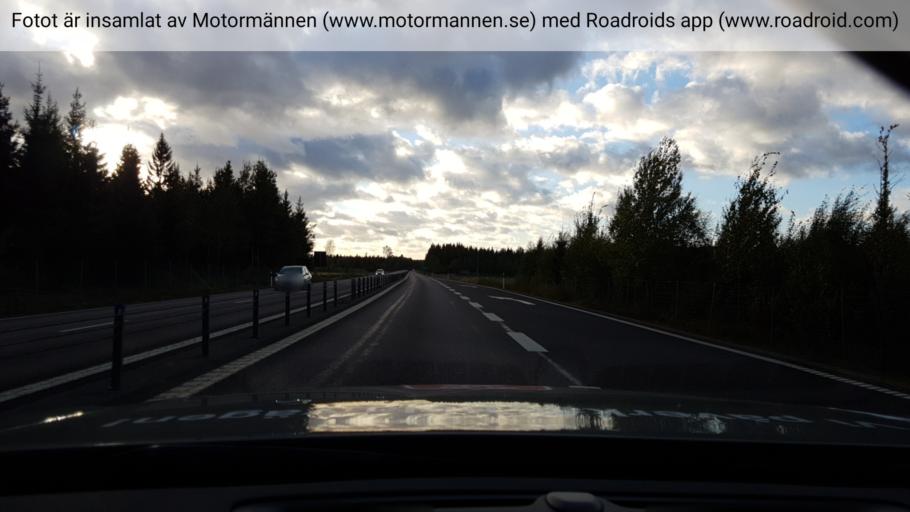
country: SE
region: Vaermland
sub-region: Karlstads Kommun
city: Skattkarr
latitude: 59.3911
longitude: 13.8459
